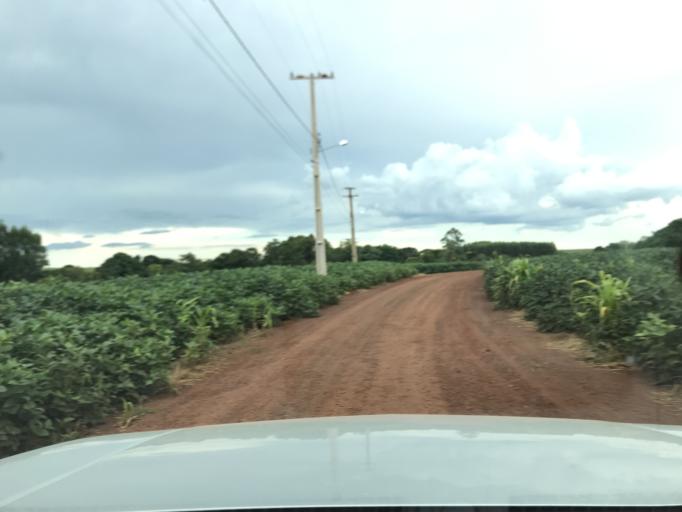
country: BR
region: Parana
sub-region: Palotina
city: Palotina
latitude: -24.2753
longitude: -53.7912
